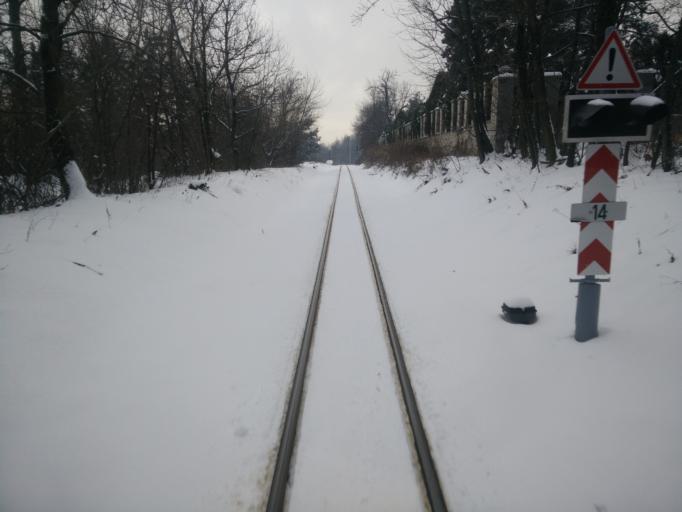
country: HU
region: Pest
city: Budaors
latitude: 47.4997
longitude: 18.9649
